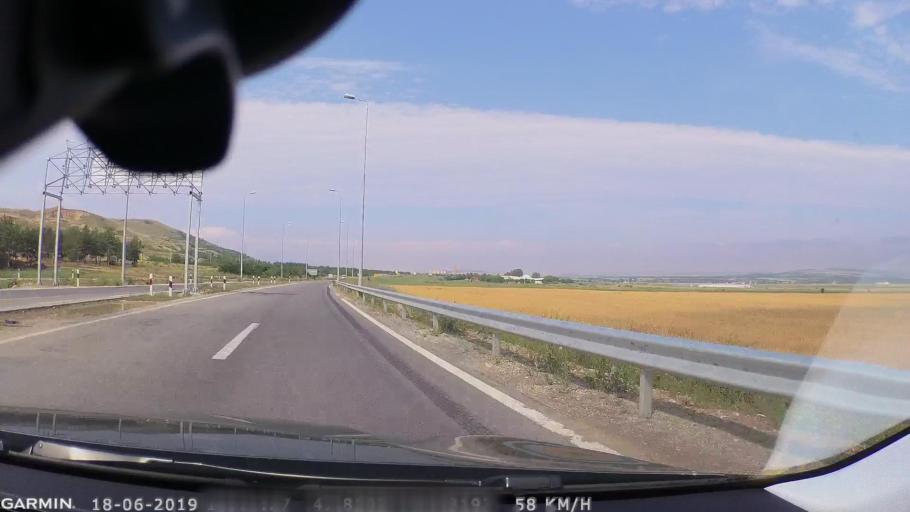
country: MK
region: Sveti Nikole
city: Sveti Nikole
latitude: 41.8287
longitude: 22.0007
